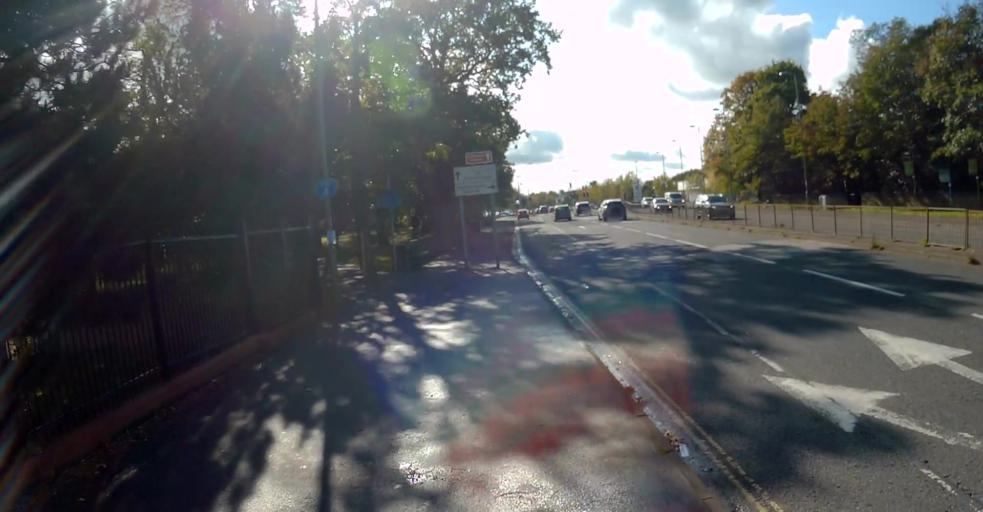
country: GB
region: England
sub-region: Hampshire
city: Farnborough
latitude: 51.2862
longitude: -0.7523
